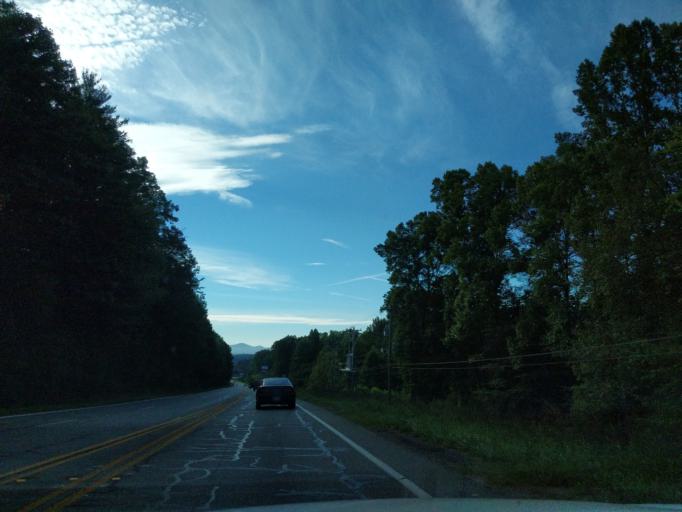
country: US
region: Georgia
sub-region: Fannin County
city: Blue Ridge
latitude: 34.9026
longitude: -84.3723
